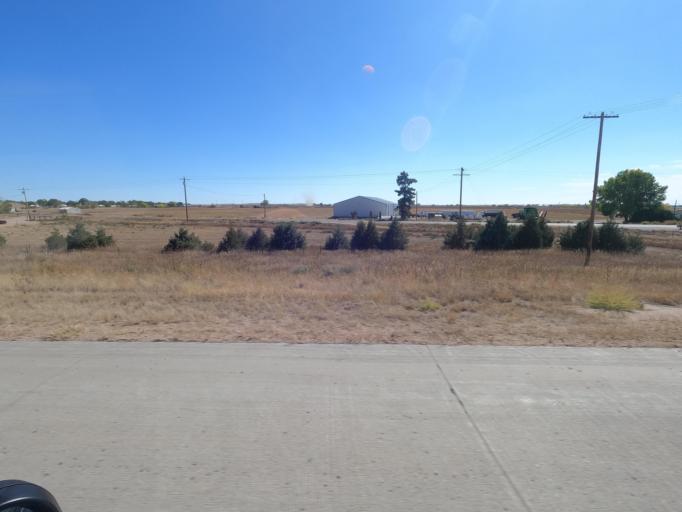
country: US
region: Colorado
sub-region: Morgan County
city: Fort Morgan
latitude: 40.2336
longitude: -104.0864
